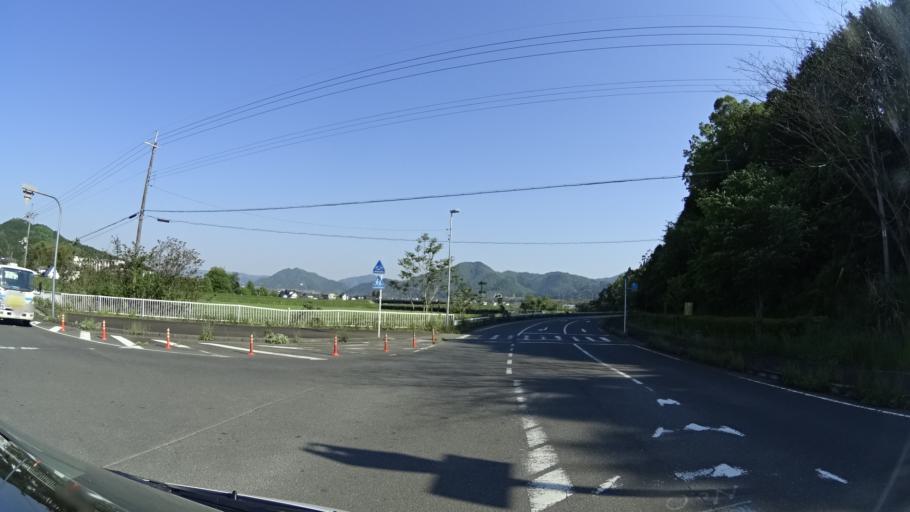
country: JP
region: Kyoto
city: Ayabe
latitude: 35.3214
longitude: 135.2091
